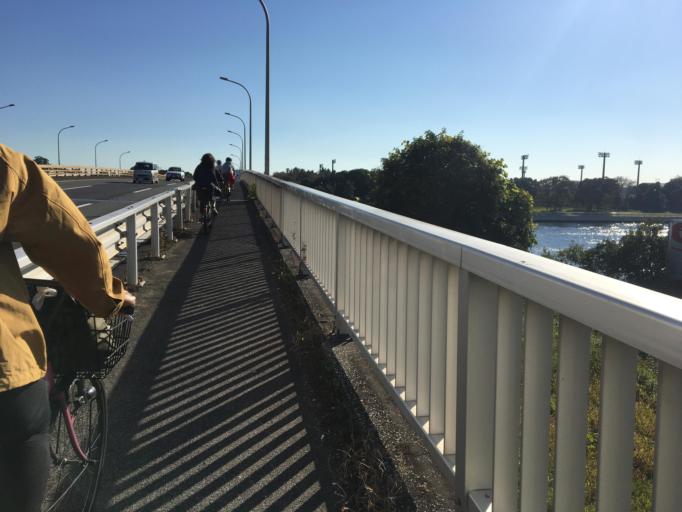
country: JP
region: Tokyo
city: Urayasu
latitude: 35.6560
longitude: 139.8240
